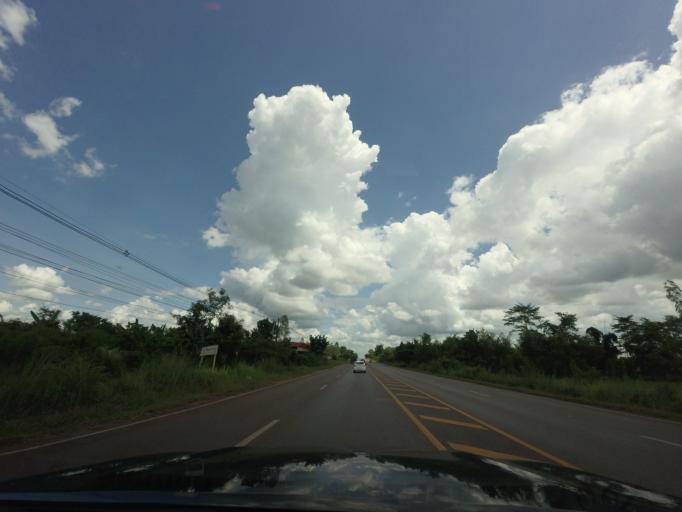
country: TH
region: Changwat Udon Thani
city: Ban Dung
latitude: 17.6851
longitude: 103.2074
